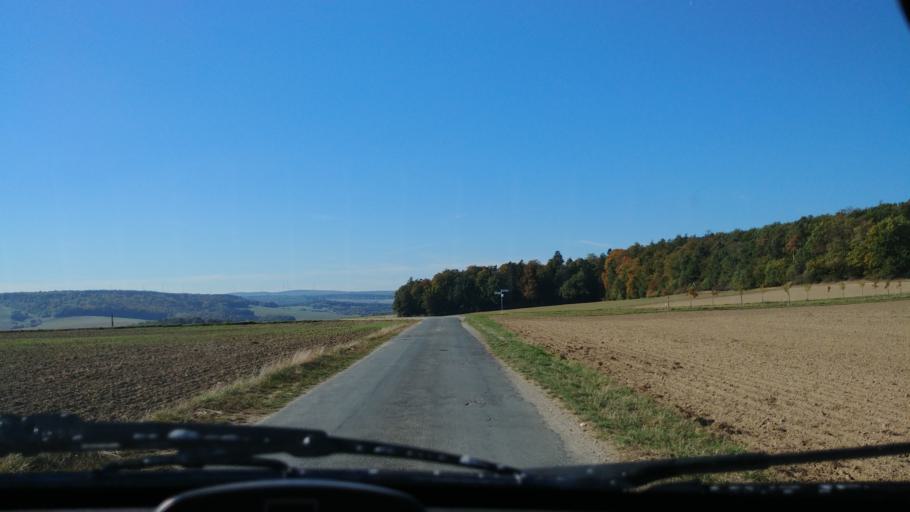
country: DE
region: Hesse
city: Burg Hohenstein
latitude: 50.2244
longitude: 8.1027
